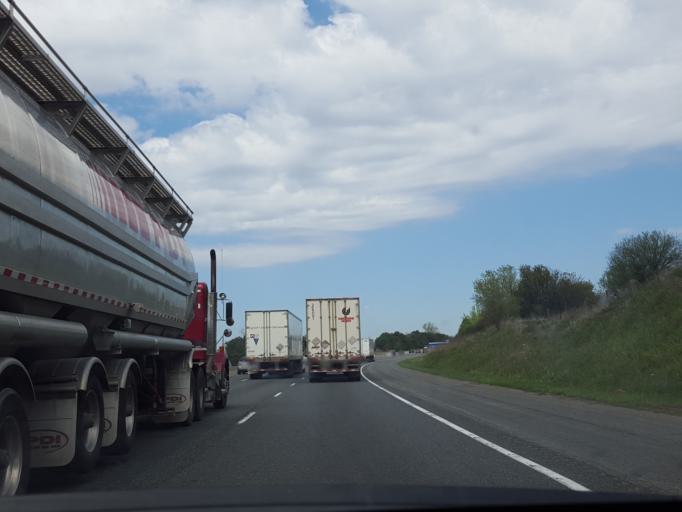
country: CA
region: Ontario
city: Oshawa
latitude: 43.8770
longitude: -78.7994
